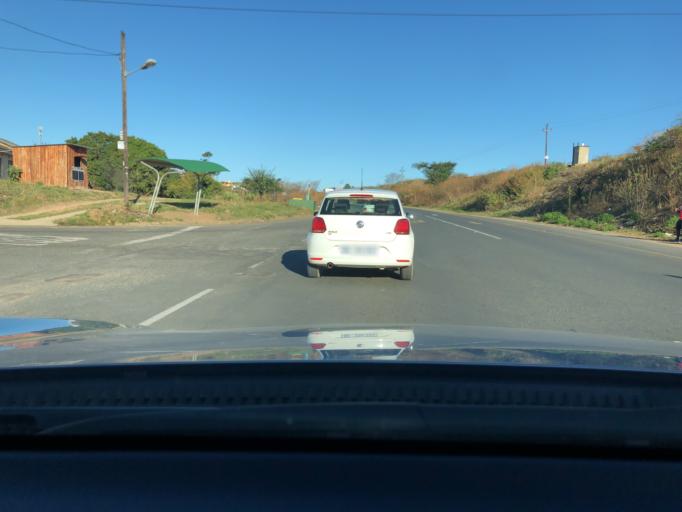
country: ZA
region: KwaZulu-Natal
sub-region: eThekwini Metropolitan Municipality
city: Umkomaas
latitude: -30.0336
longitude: 30.8340
